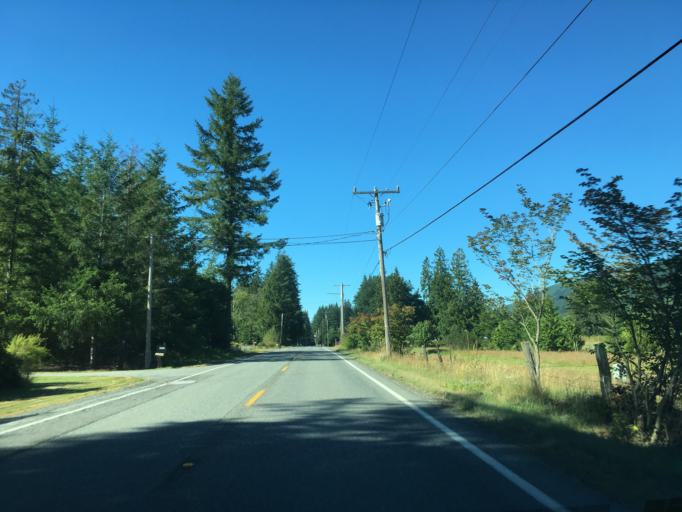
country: US
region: Washington
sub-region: Skagit County
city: Sedro-Woolley
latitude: 48.5785
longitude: -122.2244
